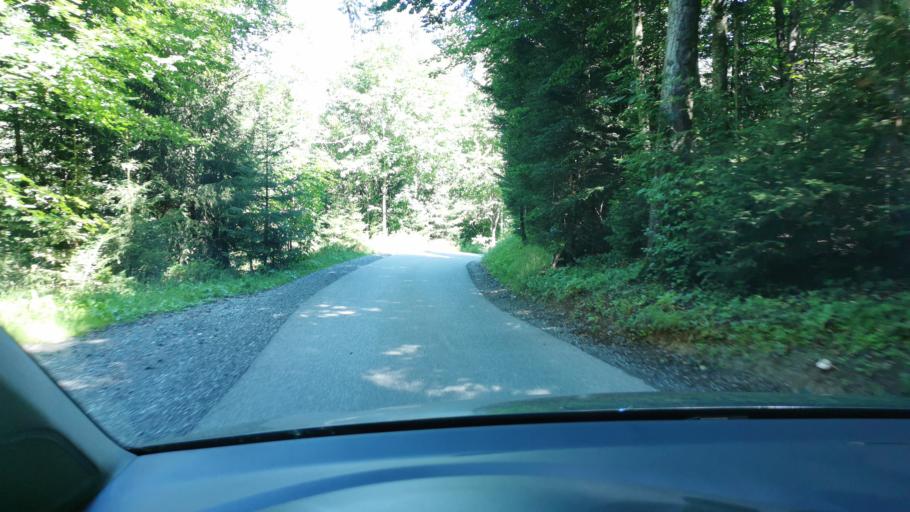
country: AT
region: Vorarlberg
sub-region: Politischer Bezirk Feldkirch
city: Viktorsberg
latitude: 47.2850
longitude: 9.6725
